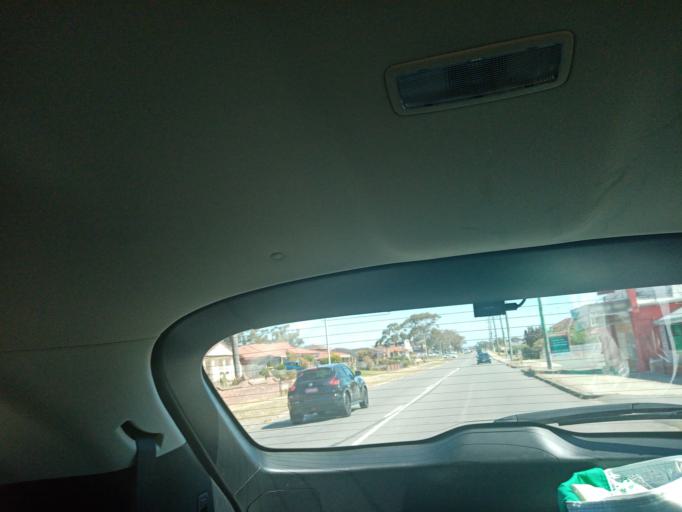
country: AU
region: Western Australia
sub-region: City of Cockburn
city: Spearwood
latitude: -32.1127
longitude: 115.7827
